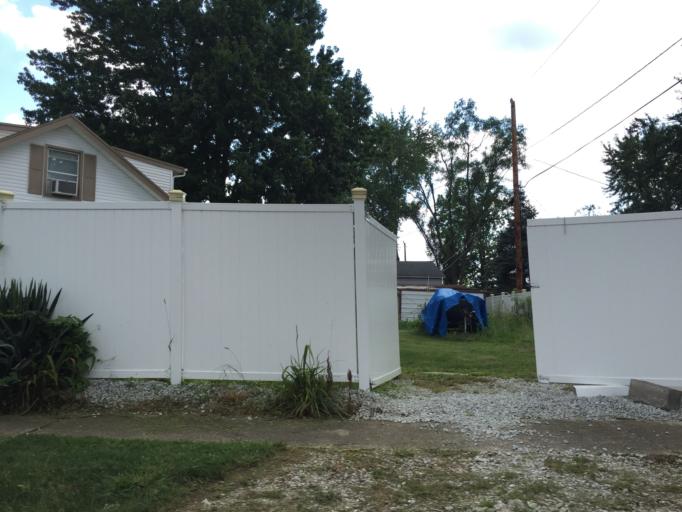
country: US
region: Indiana
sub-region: Howard County
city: Kokomo
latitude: 40.4662
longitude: -86.1038
